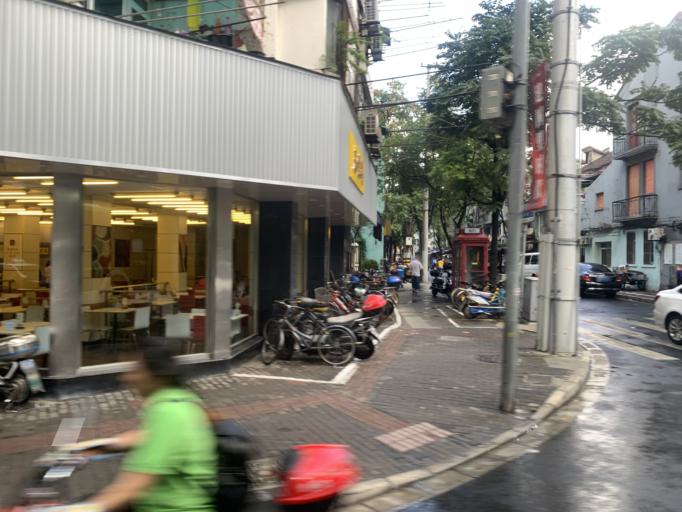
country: CN
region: Shanghai Shi
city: Luwan
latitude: 31.2137
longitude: 121.4732
